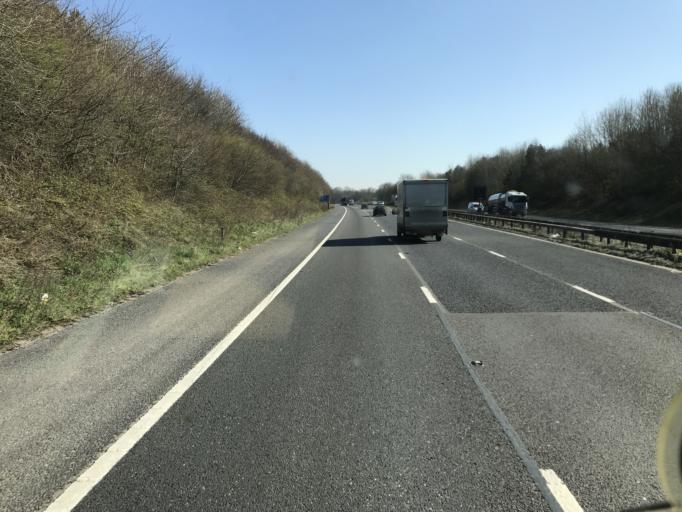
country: GB
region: England
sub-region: Borough of Halton
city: Daresbury
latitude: 53.3285
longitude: -2.6305
